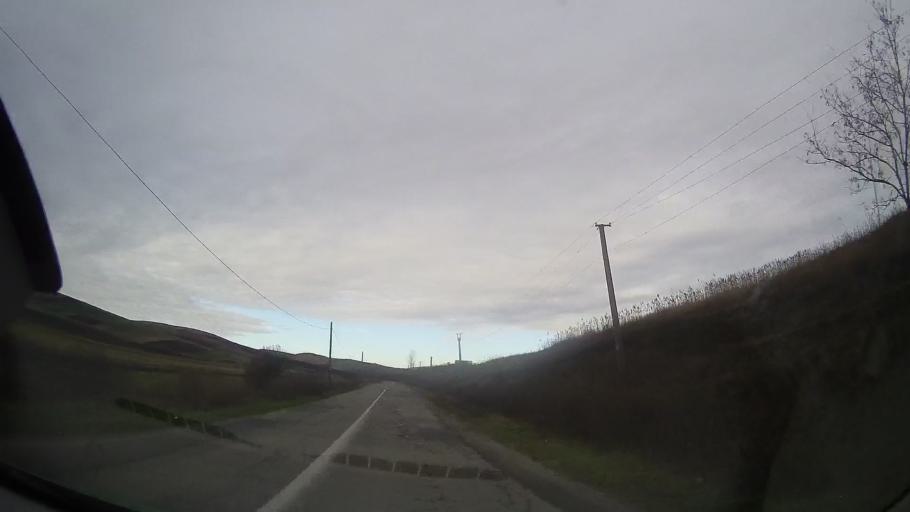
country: RO
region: Cluj
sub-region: Comuna Camarasu
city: Camarasu
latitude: 46.8045
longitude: 24.1468
